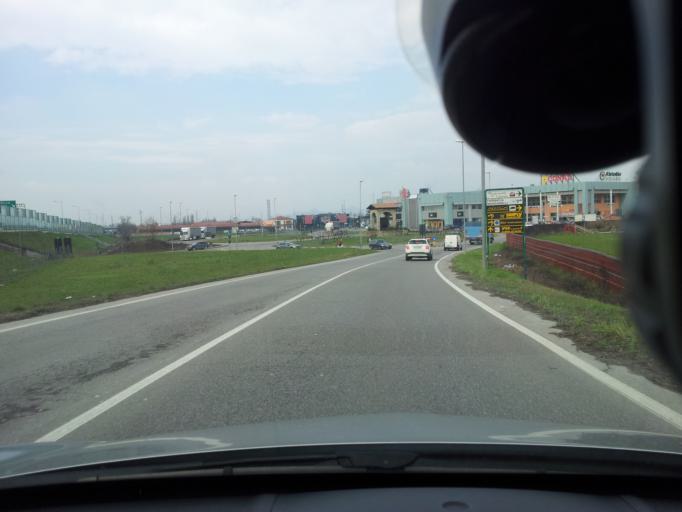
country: IT
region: Lombardy
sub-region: Provincia di Bergamo
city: Grumello del Monte
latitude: 45.6318
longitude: 9.8631
